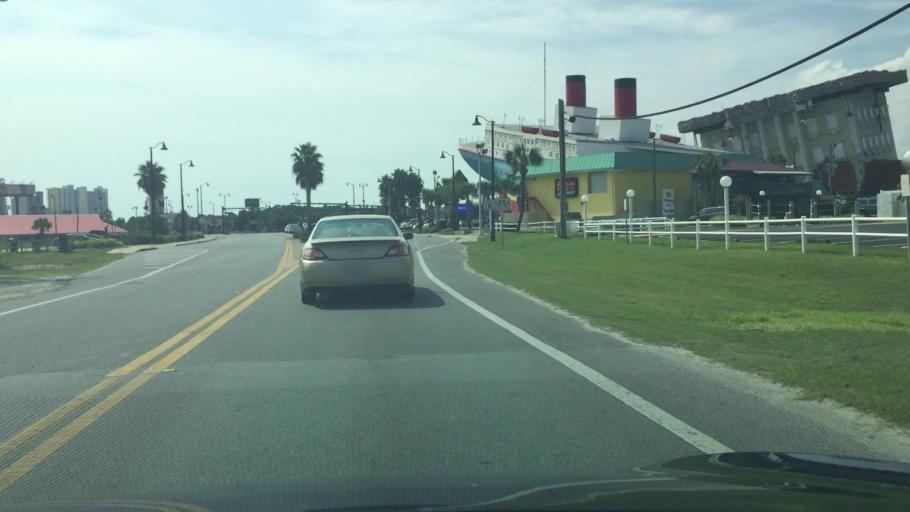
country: US
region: Florida
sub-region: Bay County
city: Panama City Beach
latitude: 30.1774
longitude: -85.7984
